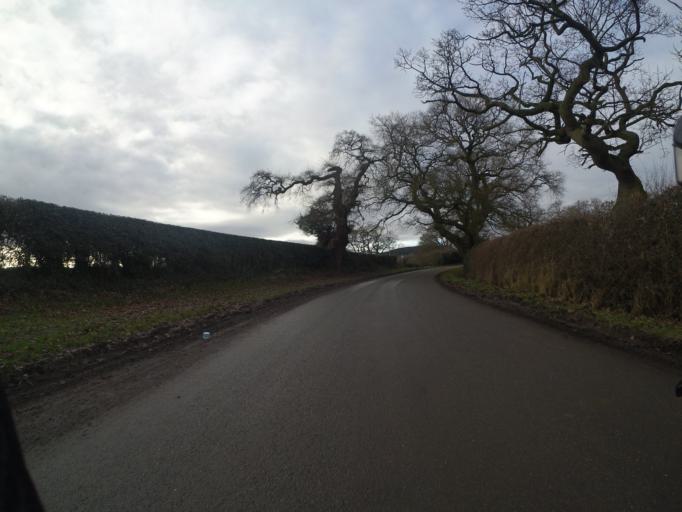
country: GB
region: England
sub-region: Cheshire West and Chester
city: Tiverton
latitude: 53.1189
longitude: -2.6688
